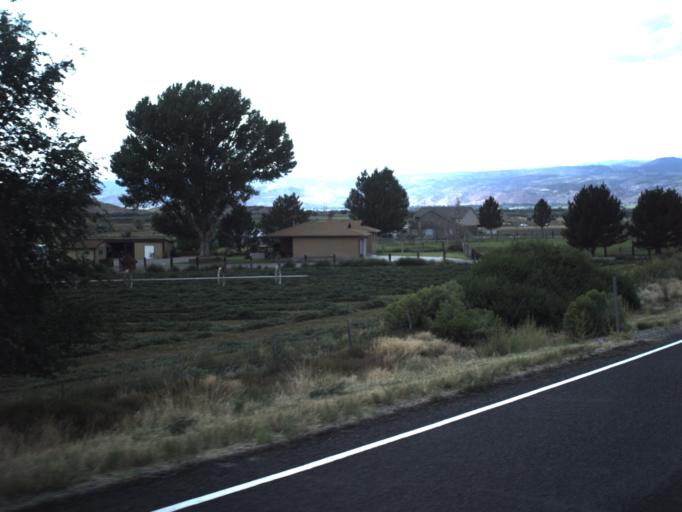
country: US
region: Utah
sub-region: Sevier County
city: Richfield
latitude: 38.7740
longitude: -111.9861
